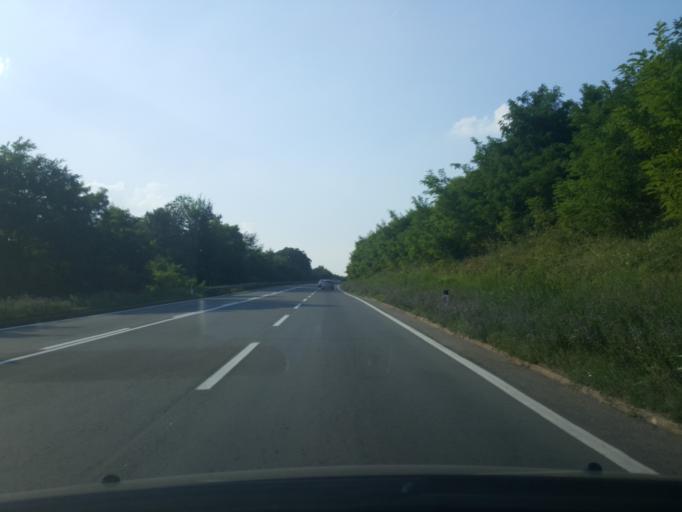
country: RS
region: Central Serbia
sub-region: Belgrade
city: Mladenovac
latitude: 44.5075
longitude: 20.6552
